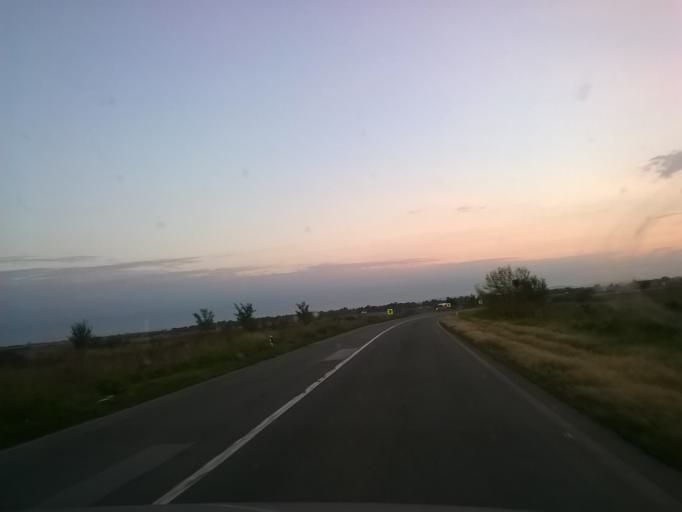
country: RS
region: Autonomna Pokrajina Vojvodina
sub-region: Juznobanatski Okrug
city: Pancevo
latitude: 44.9190
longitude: 20.6578
